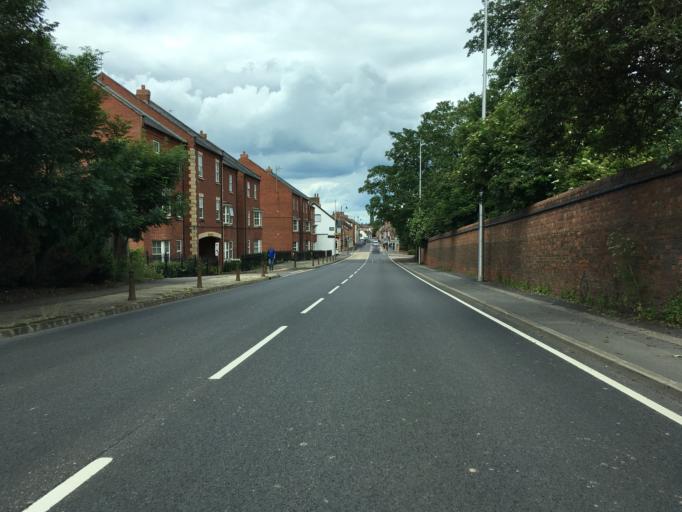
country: GB
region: England
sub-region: Northamptonshire
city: Towcester
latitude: 52.1281
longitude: -0.9830
